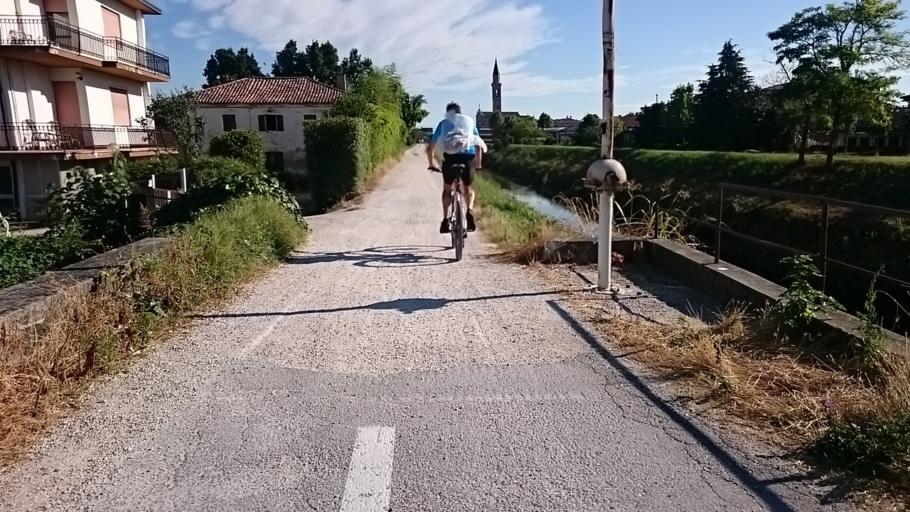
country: IT
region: Veneto
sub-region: Provincia di Padova
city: Campodarsego
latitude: 45.4975
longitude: 11.9049
